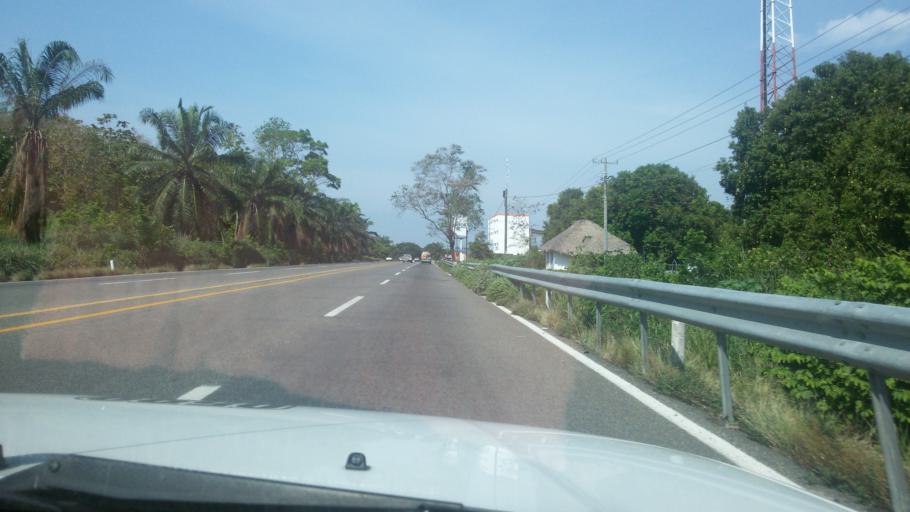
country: MX
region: Chiapas
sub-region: Tapachula
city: Vida Mejor I
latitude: 14.8301
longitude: -92.3289
